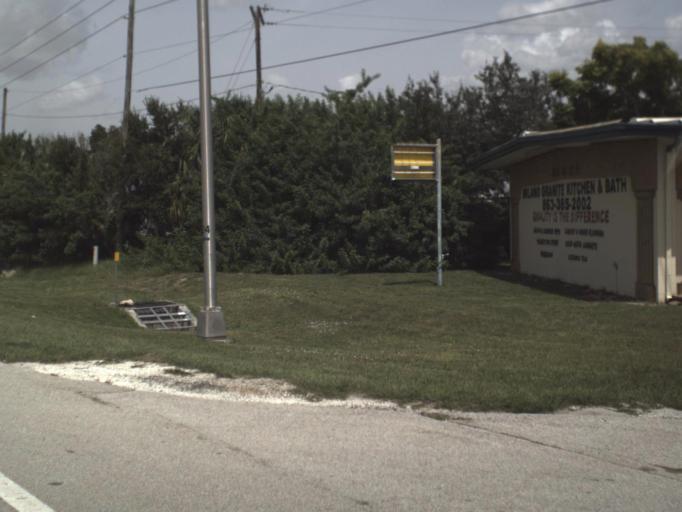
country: US
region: Florida
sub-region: Highlands County
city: Sebring
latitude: 27.4923
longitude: -81.4847
